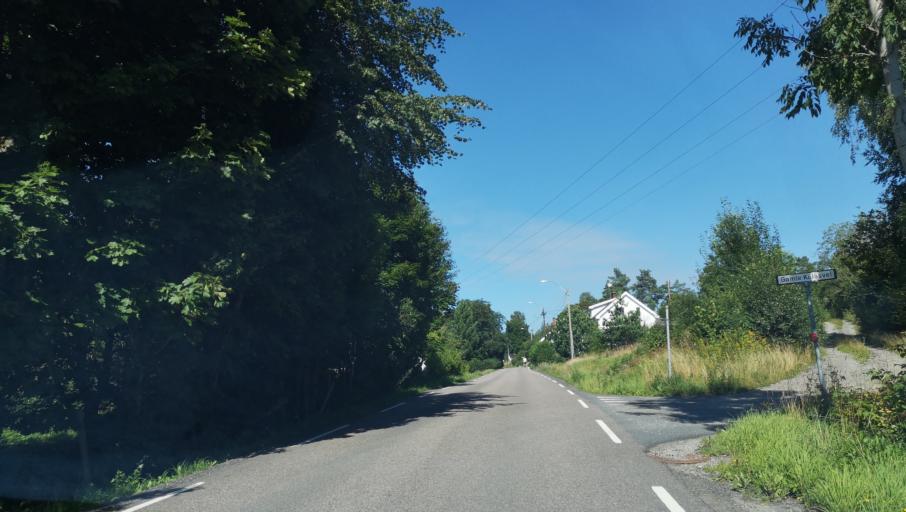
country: NO
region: Akershus
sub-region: Vestby
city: Vestby
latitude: 59.5342
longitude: 10.6891
